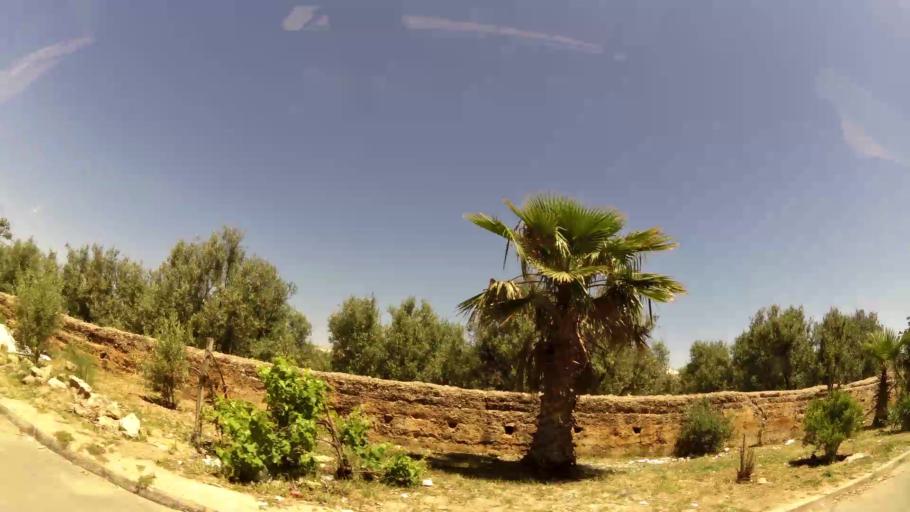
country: MA
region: Meknes-Tafilalet
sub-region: Meknes
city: Meknes
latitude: 33.8552
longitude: -5.5567
